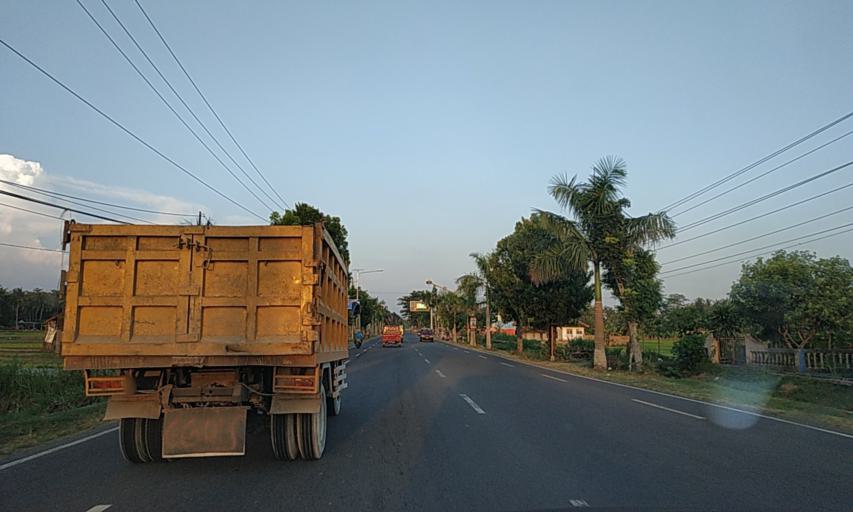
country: ID
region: Daerah Istimewa Yogyakarta
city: Srandakan
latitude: -7.8883
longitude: 110.0943
